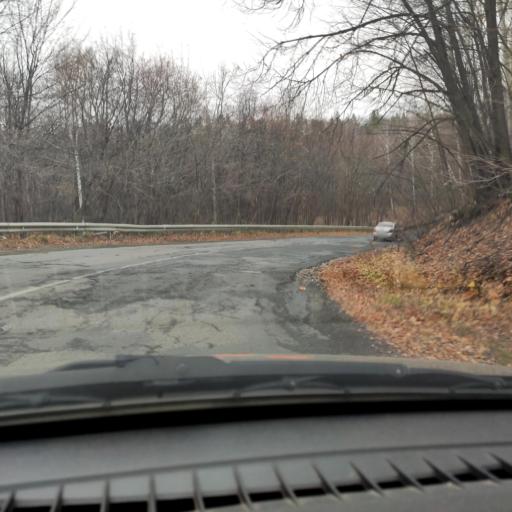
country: RU
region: Samara
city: Zhigulevsk
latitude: 53.4118
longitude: 49.6538
